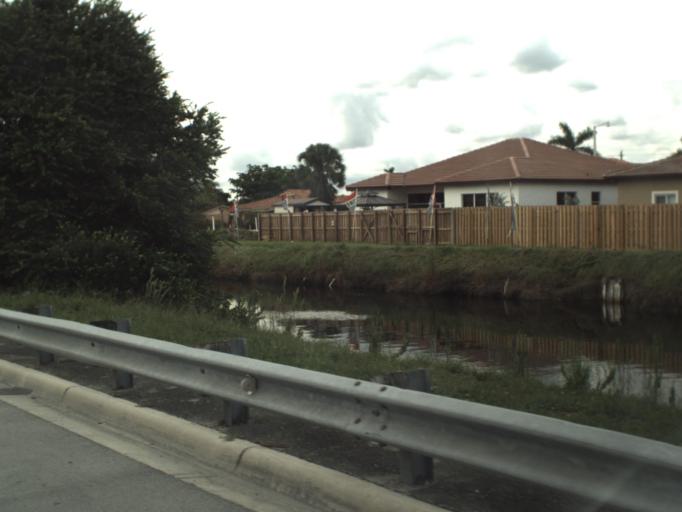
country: US
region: Florida
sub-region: Miami-Dade County
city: Sweetwater
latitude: 25.7616
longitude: -80.3626
